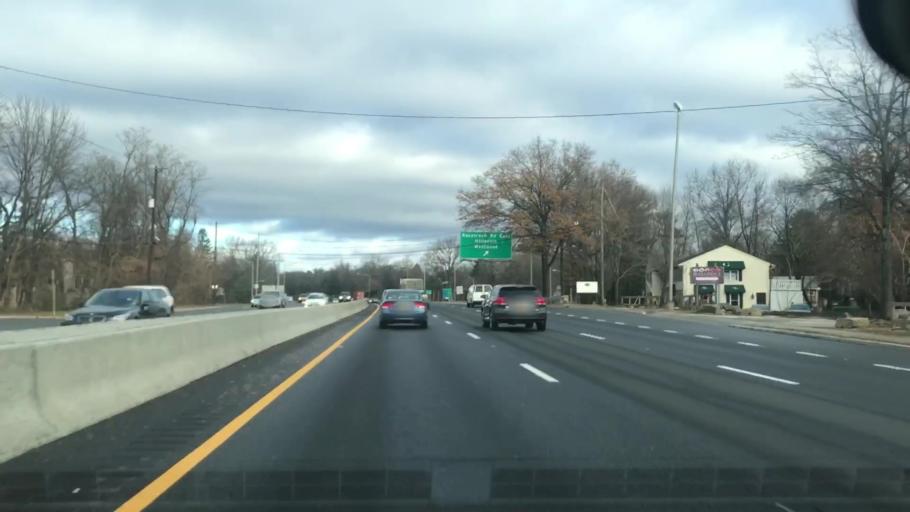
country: US
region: New Jersey
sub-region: Bergen County
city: Ho-Ho-Kus
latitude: 40.9915
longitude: -74.0956
